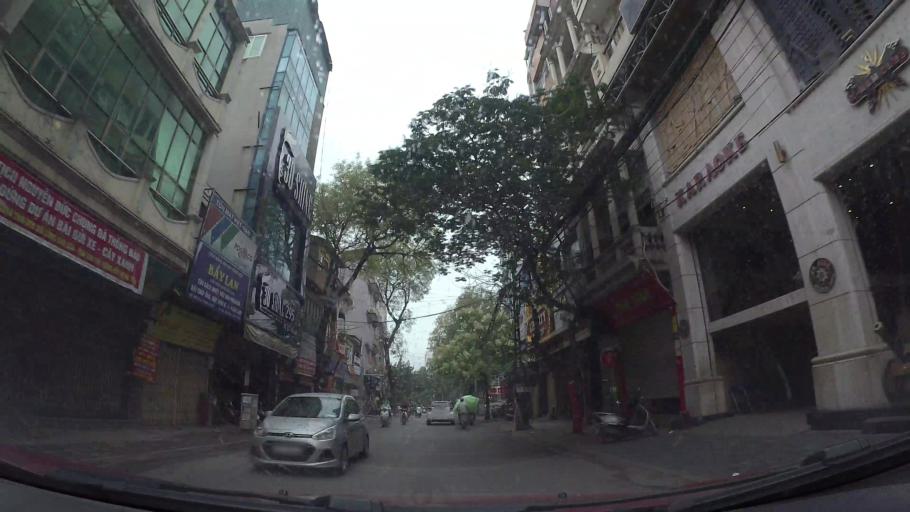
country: VN
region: Ha Noi
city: Dong Da
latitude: 21.0226
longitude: 105.8229
